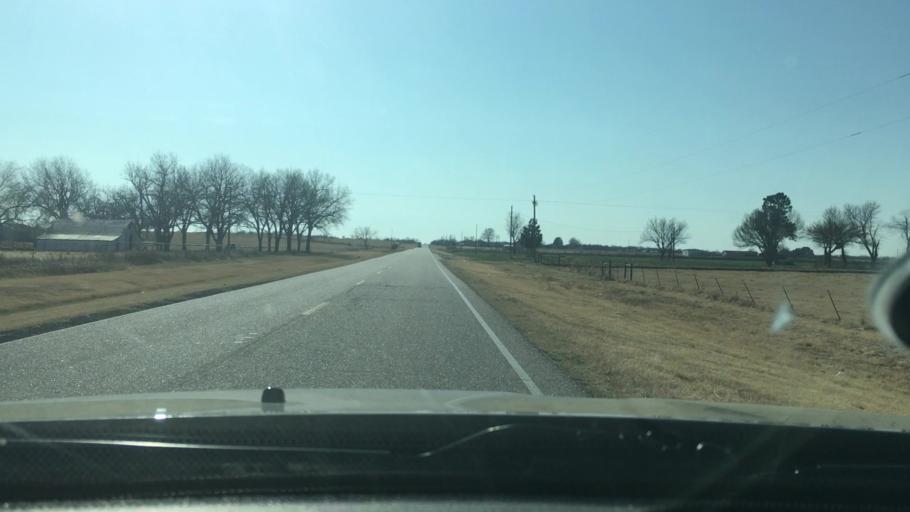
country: US
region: Oklahoma
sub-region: Garvin County
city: Stratford
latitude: 34.8448
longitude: -96.9677
